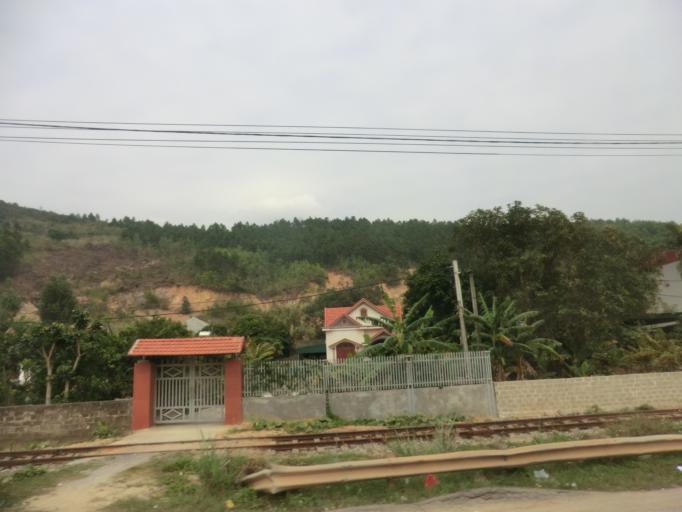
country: VN
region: Quang Ninh
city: Troi
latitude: 20.9670
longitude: 106.9369
